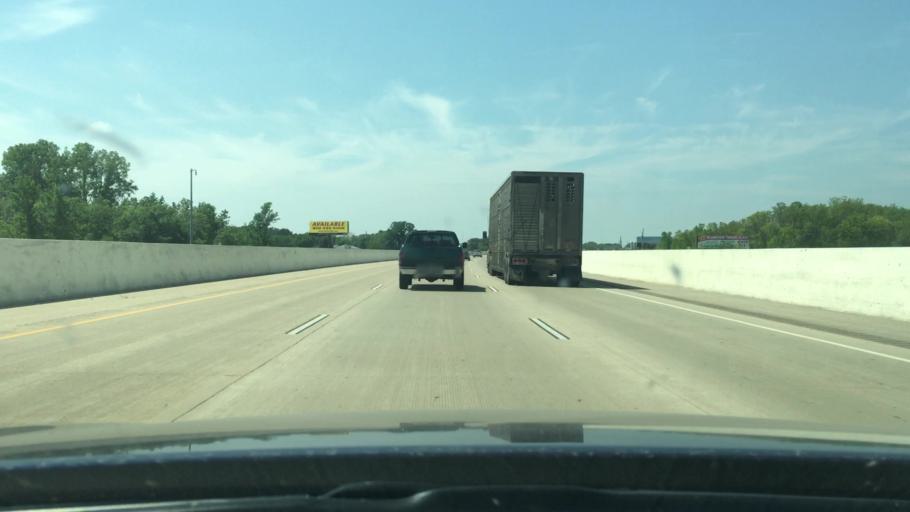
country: US
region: Wisconsin
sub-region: Winnebago County
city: Neenah
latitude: 44.1255
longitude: -88.5002
